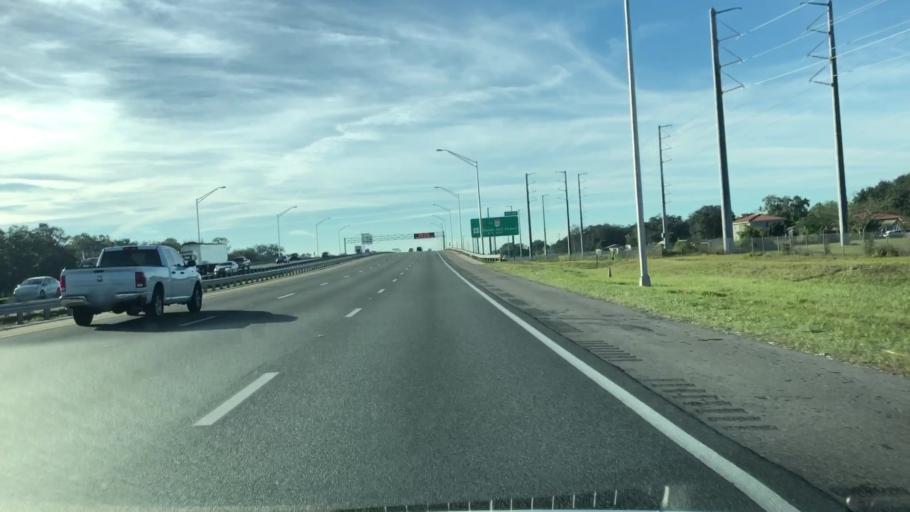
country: US
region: Florida
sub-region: Orange County
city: Azalea Park
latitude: 28.5282
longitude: -81.2510
